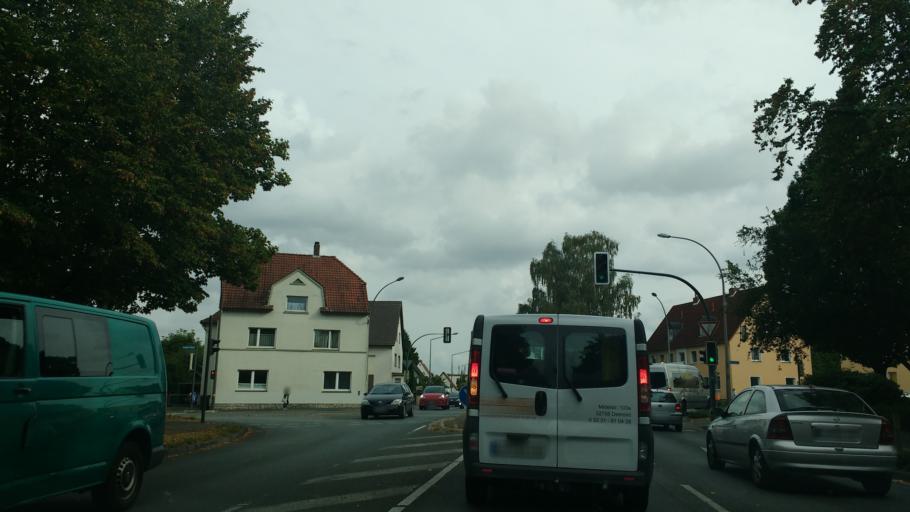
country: DE
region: North Rhine-Westphalia
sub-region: Regierungsbezirk Detmold
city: Detmold
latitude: 51.9495
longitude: 8.8790
